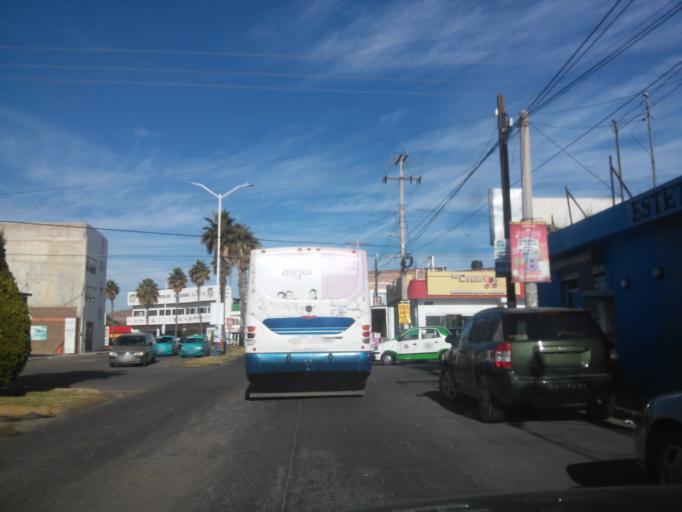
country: MX
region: Durango
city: Victoria de Durango
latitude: 24.0399
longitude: -104.6564
